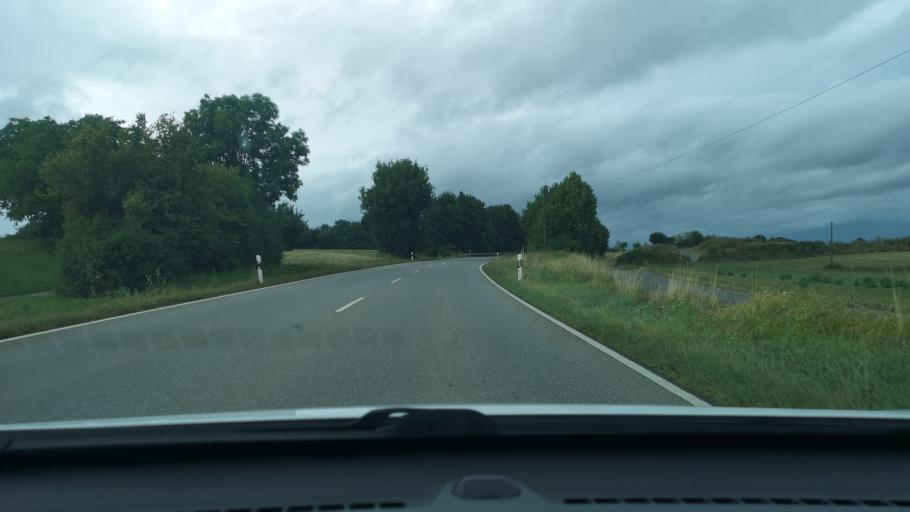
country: DE
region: Baden-Wuerttemberg
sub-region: Freiburg Region
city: Vohringen
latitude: 48.3011
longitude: 8.6262
